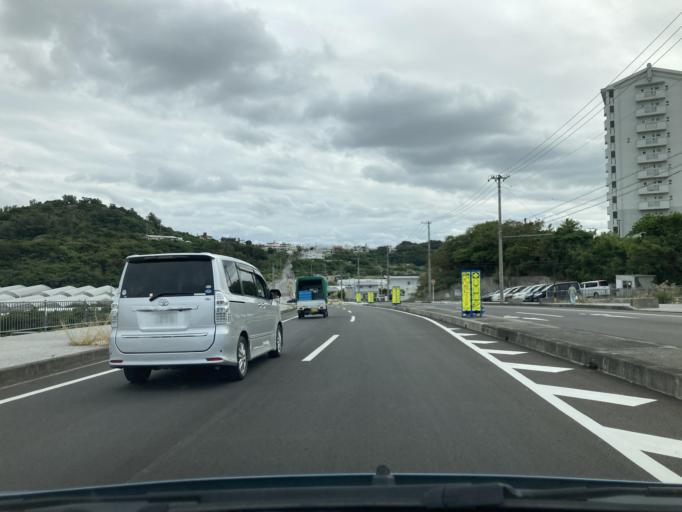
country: JP
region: Okinawa
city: Tomigusuku
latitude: 26.1678
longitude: 127.6775
